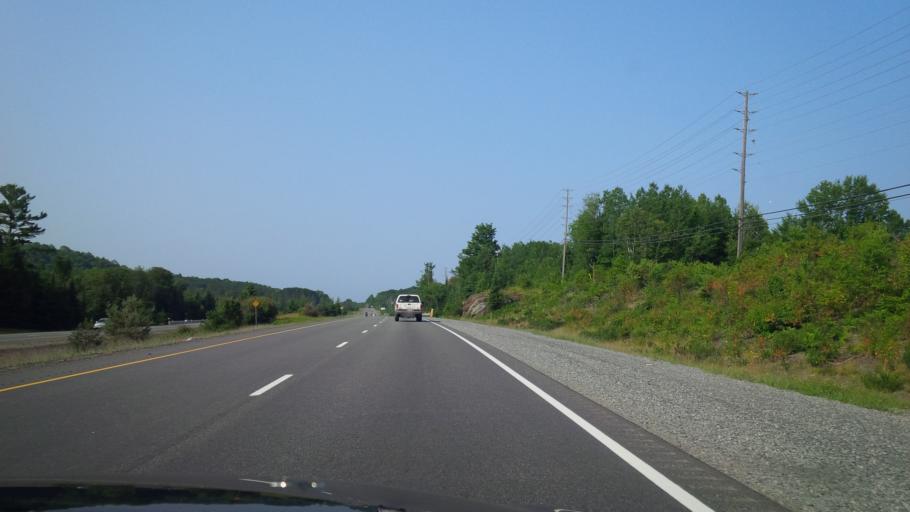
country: CA
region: Ontario
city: Huntsville
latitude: 45.2966
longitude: -79.2612
